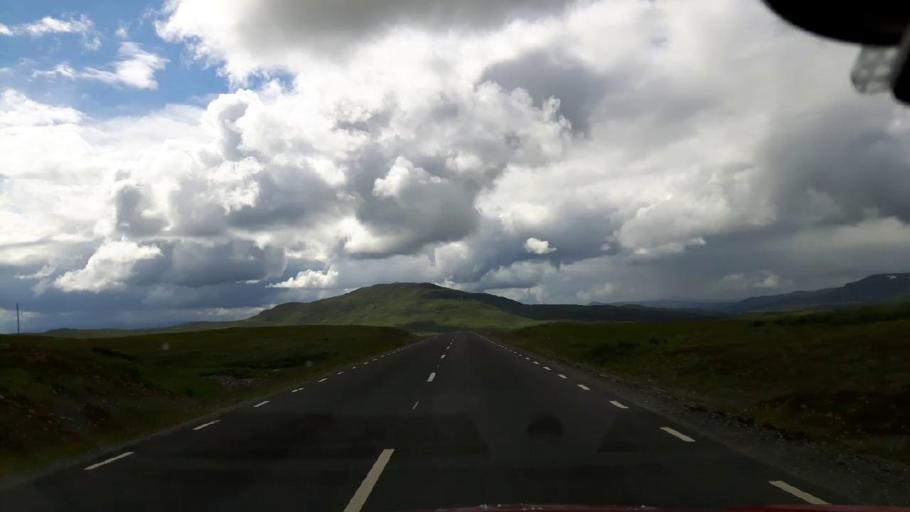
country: NO
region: Nordland
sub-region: Hattfjelldal
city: Hattfjelldal
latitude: 65.0415
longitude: 14.3285
